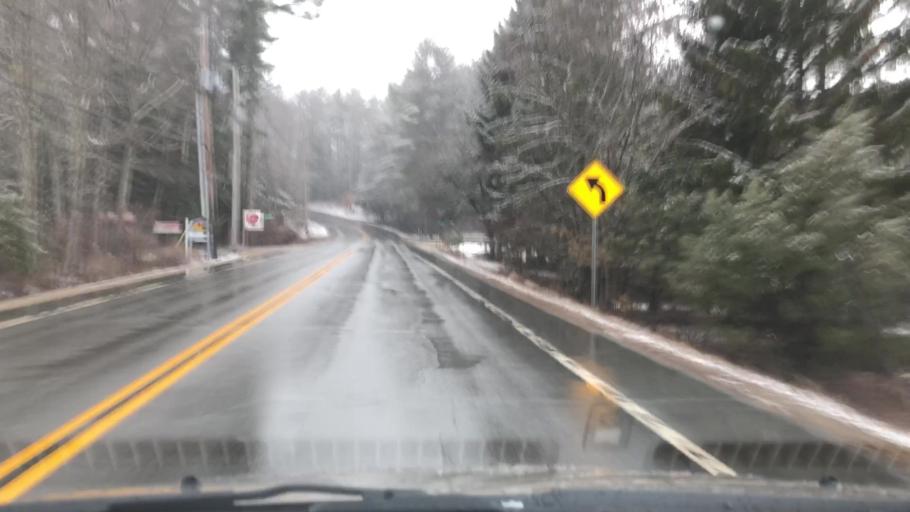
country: US
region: New Hampshire
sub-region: Strafford County
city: Madbury
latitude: 43.1578
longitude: -70.9671
